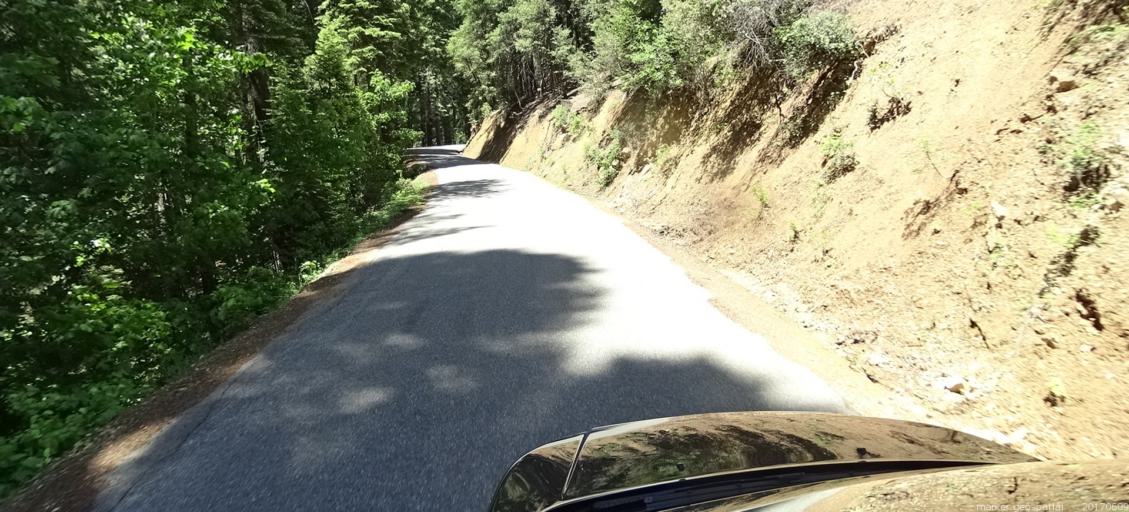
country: US
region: California
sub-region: Siskiyou County
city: Yreka
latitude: 41.3770
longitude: -123.0189
